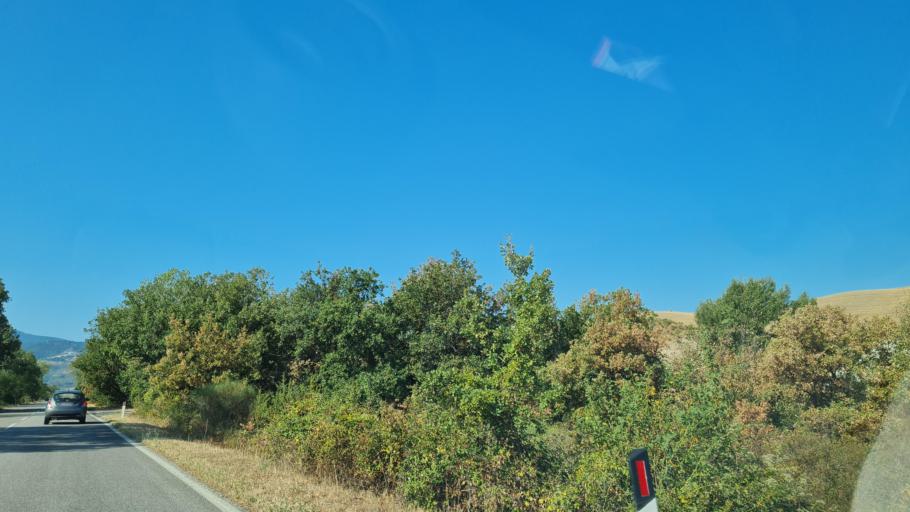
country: IT
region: Tuscany
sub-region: Provincia di Siena
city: Pienza
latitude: 42.9939
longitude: 11.7217
